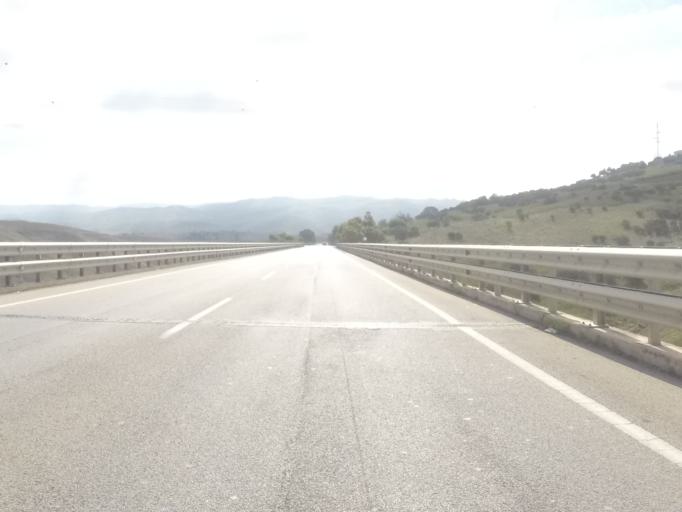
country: IT
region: Sicily
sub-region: Provincia di Caltanissetta
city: Caltanissetta
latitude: 37.4740
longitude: 14.0896
